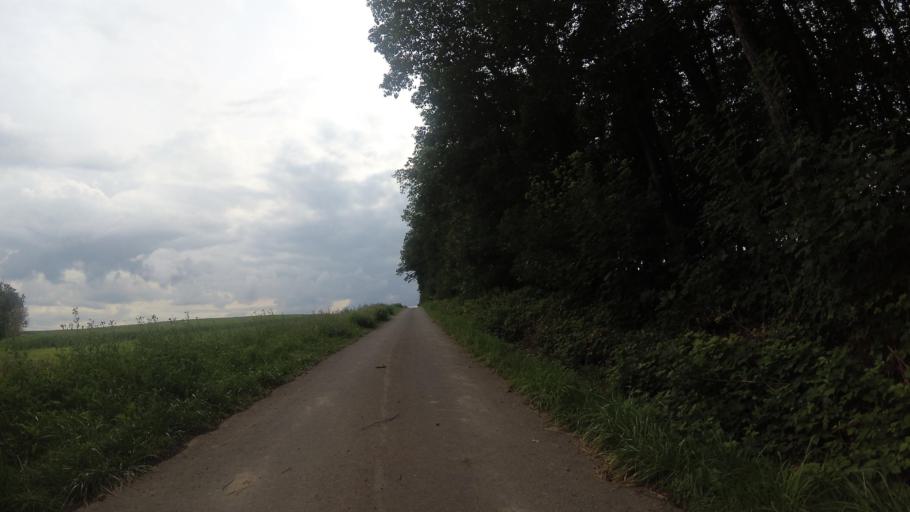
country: DE
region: Rheinland-Pfalz
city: Selchenbach
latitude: 49.4909
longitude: 7.3017
